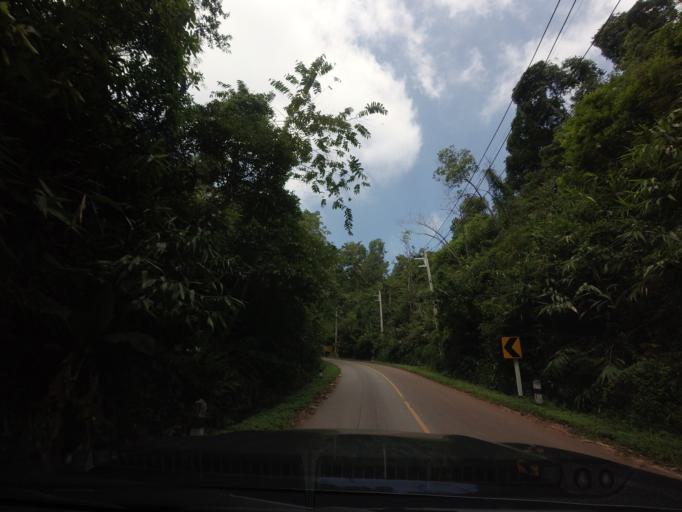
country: TH
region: Loei
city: Na Haeo
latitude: 17.4832
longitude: 100.9105
